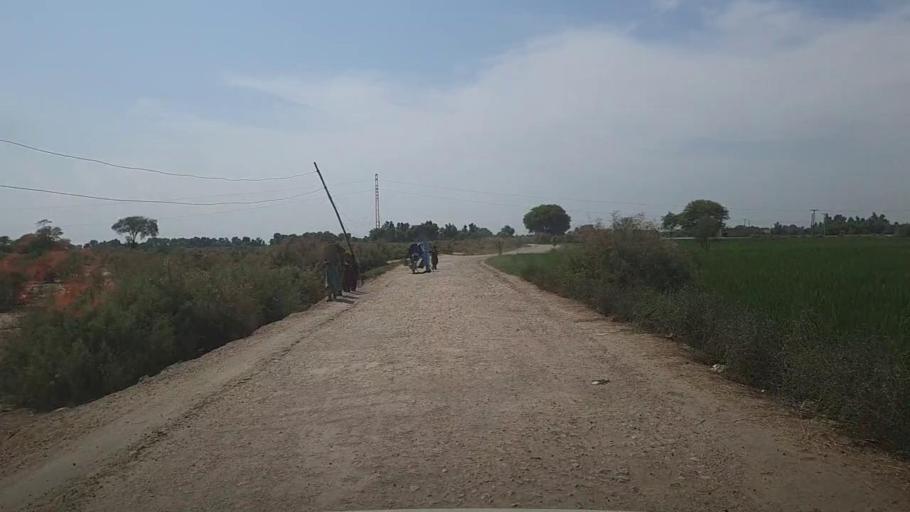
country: PK
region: Sindh
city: Kandhkot
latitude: 28.3101
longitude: 69.2042
